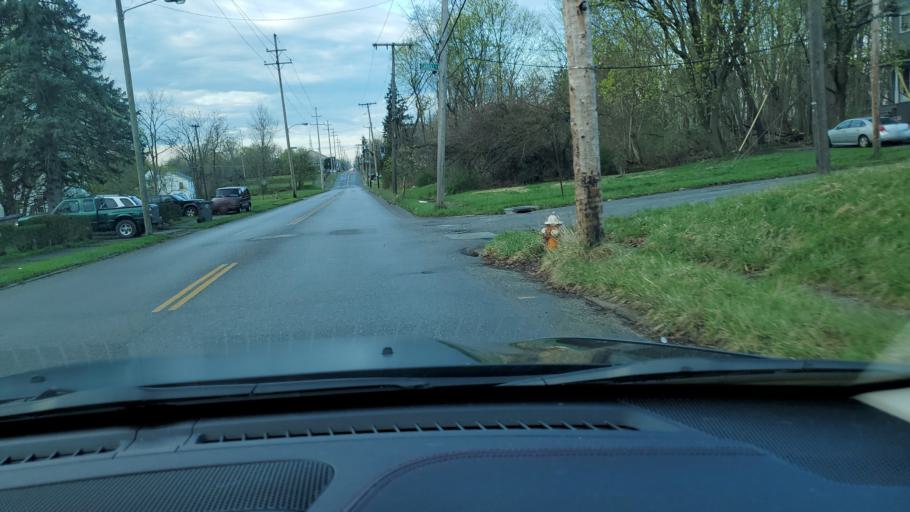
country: US
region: Ohio
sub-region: Mahoning County
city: Youngstown
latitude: 41.0905
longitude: -80.6641
